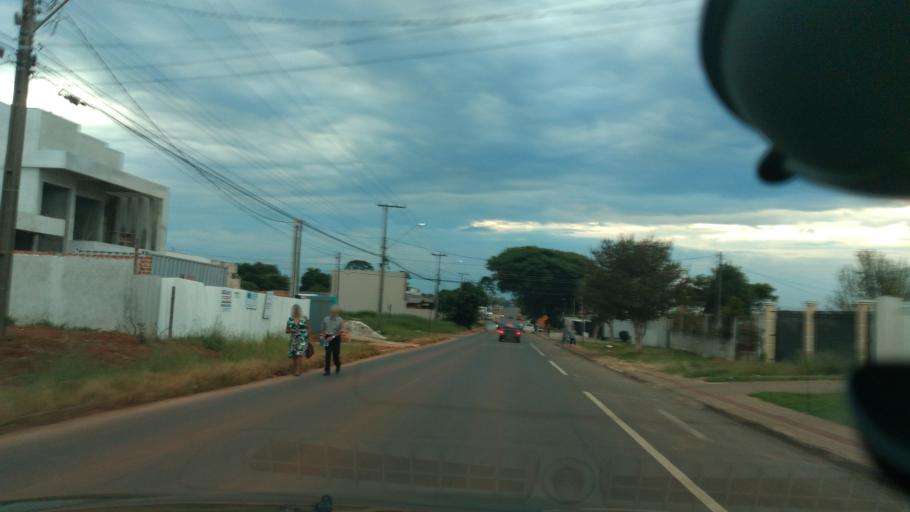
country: BR
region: Parana
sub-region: Guarapuava
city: Guarapuava
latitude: -25.3923
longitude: -51.4903
